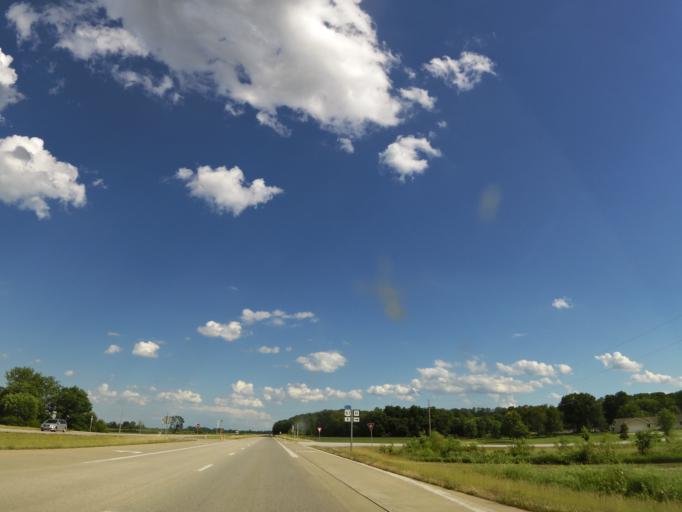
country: US
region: Illinois
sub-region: Hancock County
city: Warsaw
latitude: 40.3271
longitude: -91.5838
